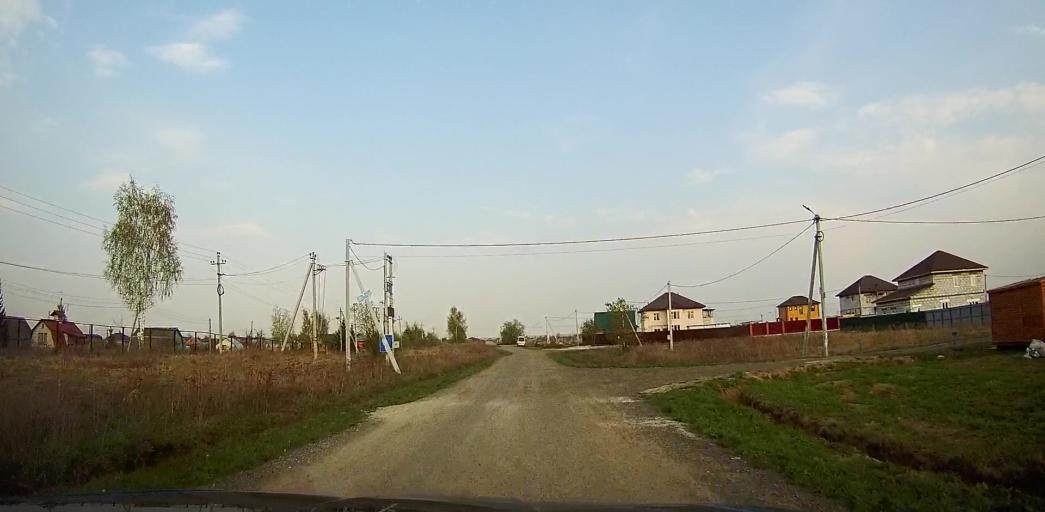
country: RU
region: Moskovskaya
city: Andreyevskoye
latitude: 55.5507
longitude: 37.9412
